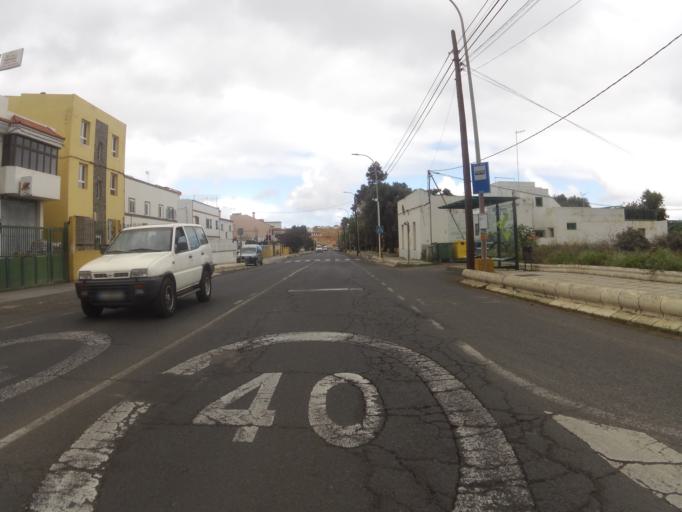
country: ES
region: Canary Islands
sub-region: Provincia de Las Palmas
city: Valsequillo de Gran Canaria
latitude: 27.9949
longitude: -15.4772
